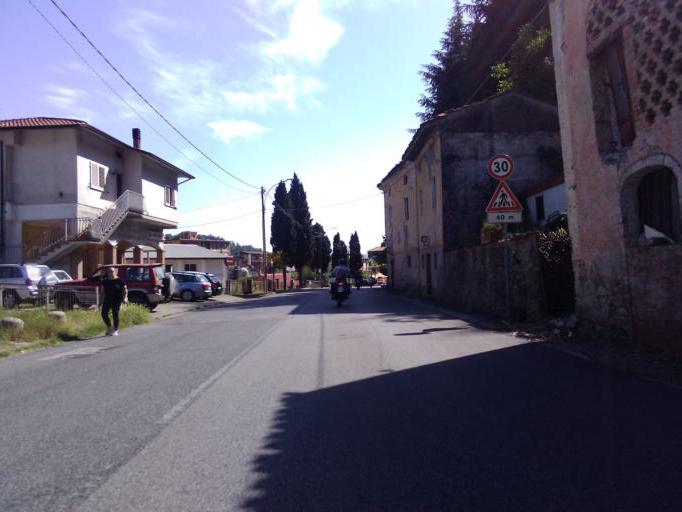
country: IT
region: Tuscany
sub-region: Provincia di Massa-Carrara
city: Licciana Nardi
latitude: 44.2668
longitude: 10.0406
